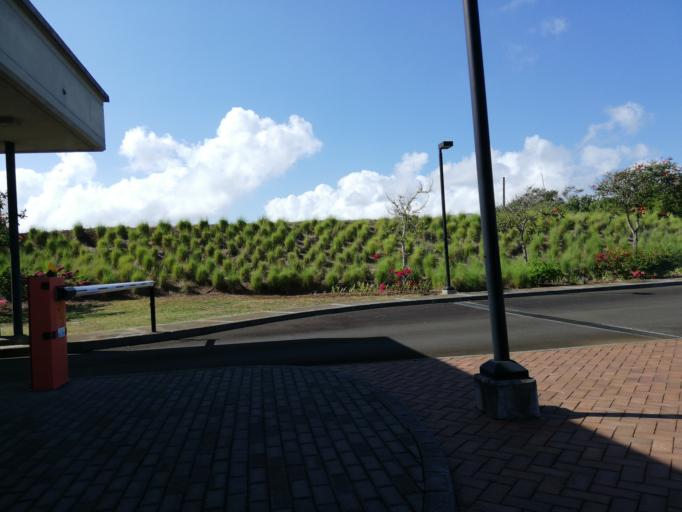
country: MU
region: Moka
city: Moka
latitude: -20.2214
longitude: 57.4936
